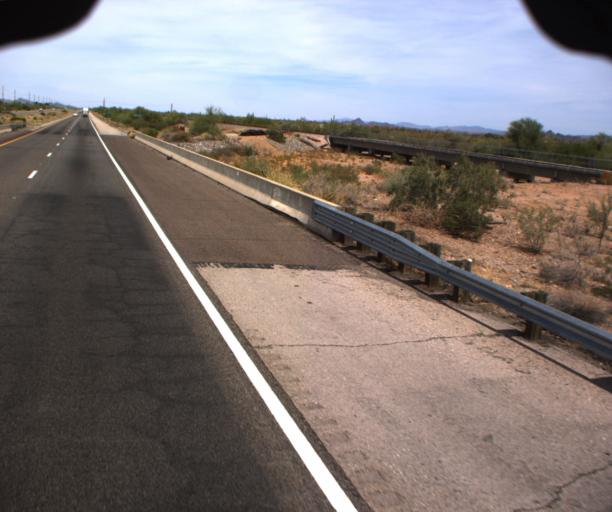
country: US
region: Arizona
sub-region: Maricopa County
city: Wickenburg
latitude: 33.8126
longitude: -112.5730
